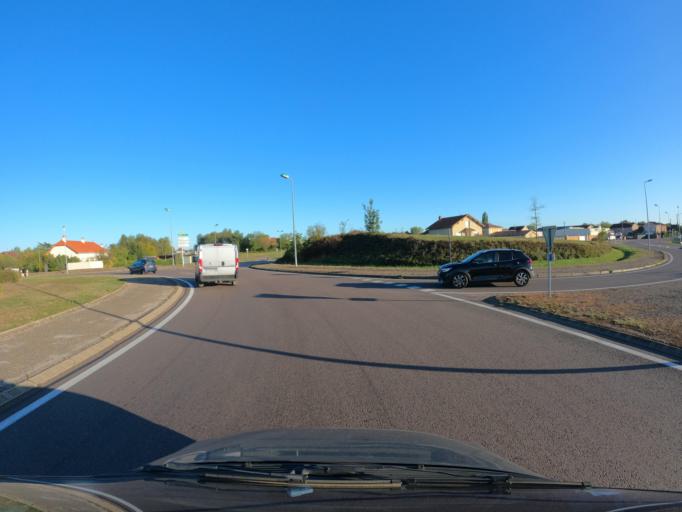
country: FR
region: Bourgogne
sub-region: Departement de Saone-et-Loire
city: Saint-Marcel
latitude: 46.7847
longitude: 4.9086
